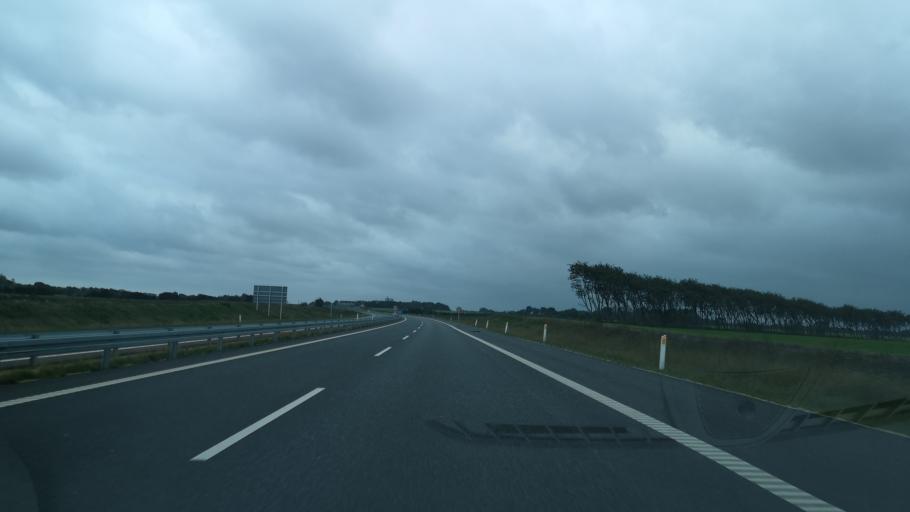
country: DK
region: Central Jutland
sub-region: Herning Kommune
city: Snejbjerg
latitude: 56.1459
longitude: 8.8699
